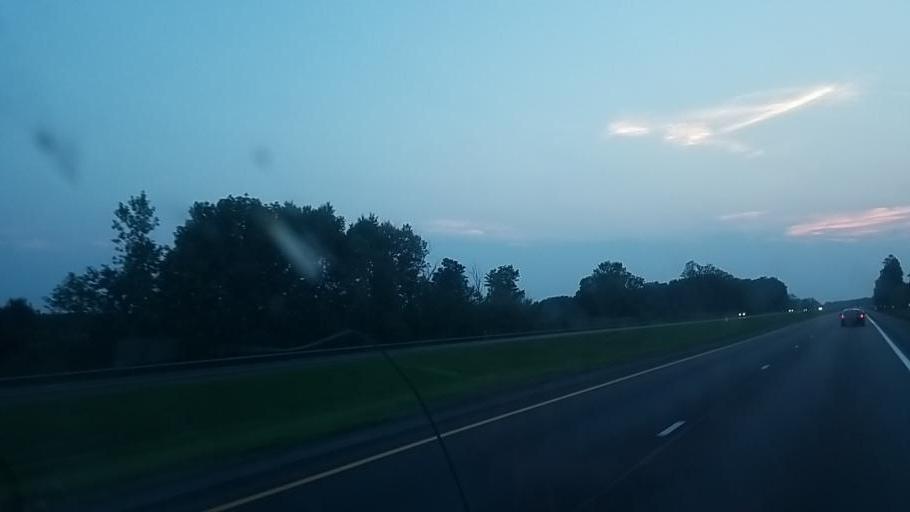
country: US
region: New York
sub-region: Oneida County
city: Rome
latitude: 43.1317
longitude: -75.4591
